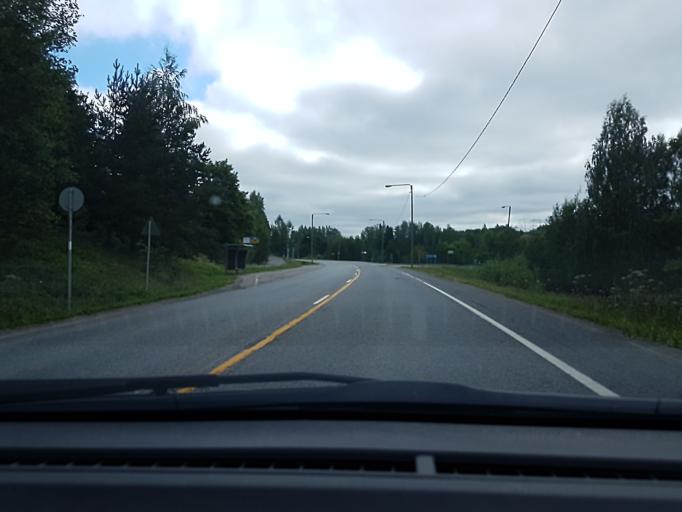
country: FI
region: Uusimaa
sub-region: Helsinki
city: Kerava
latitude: 60.3582
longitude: 25.1755
